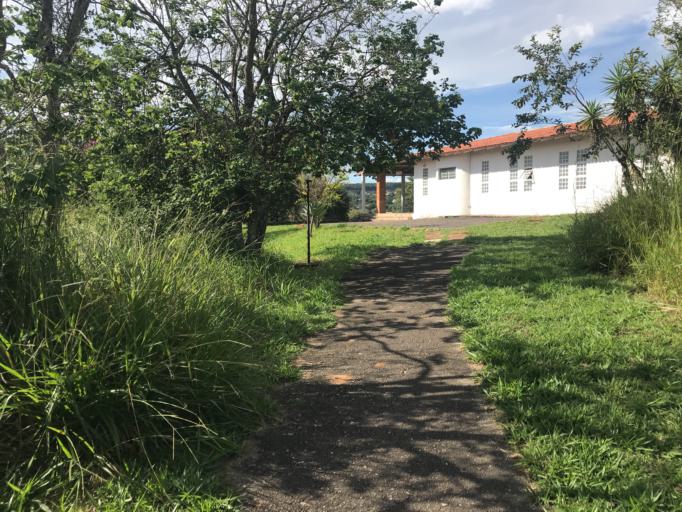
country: BR
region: Federal District
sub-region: Brasilia
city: Brasilia
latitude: -15.7967
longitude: -47.8014
